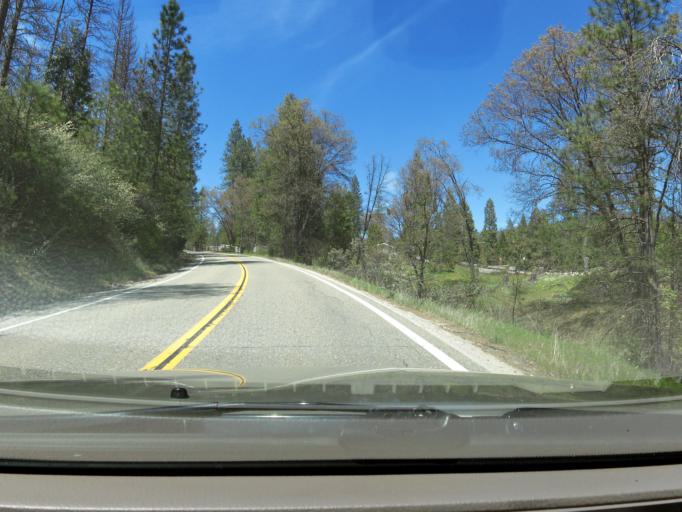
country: US
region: California
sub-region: Madera County
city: Oakhurst
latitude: 37.2636
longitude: -119.5728
